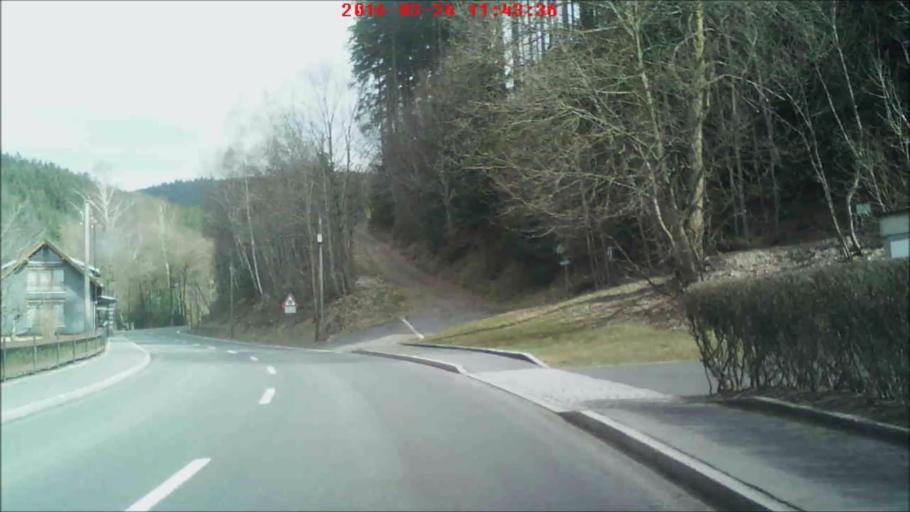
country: DE
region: Thuringia
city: Bachfeld
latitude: 50.4507
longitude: 10.9735
